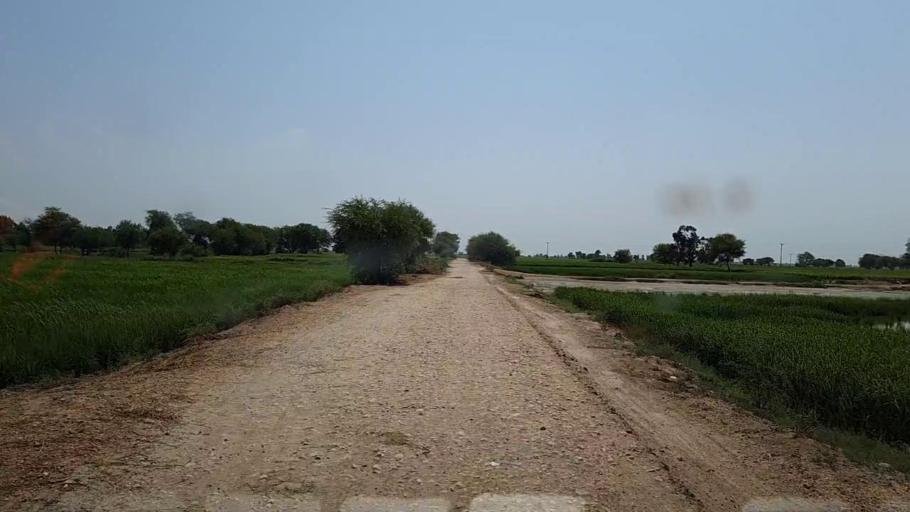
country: PK
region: Sindh
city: Kario
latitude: 24.6425
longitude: 68.4860
